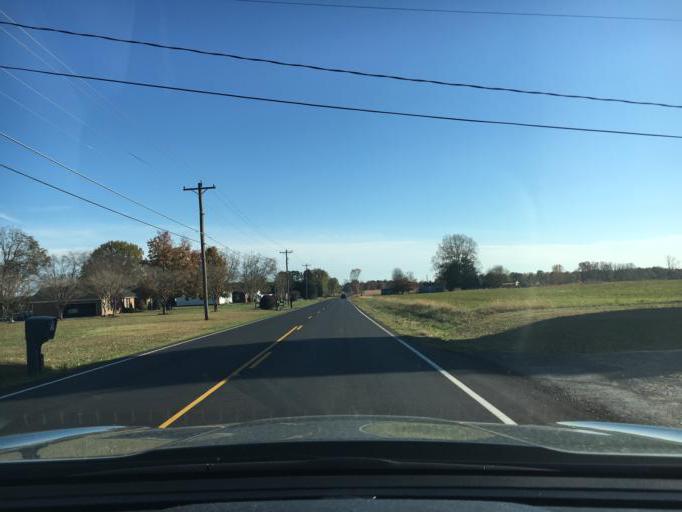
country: US
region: South Carolina
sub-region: Spartanburg County
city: Inman Mills
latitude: 35.0468
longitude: -82.1368
